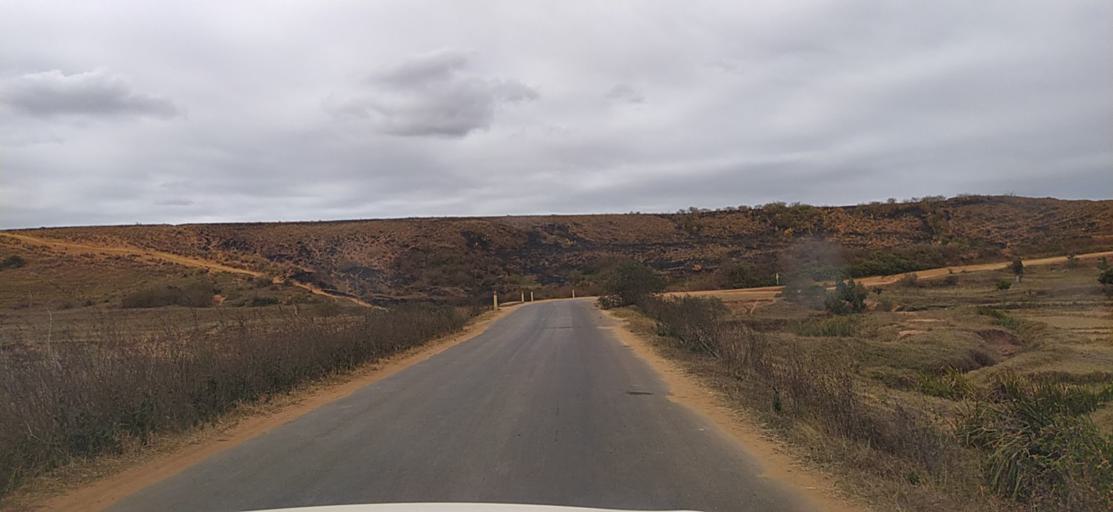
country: MG
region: Alaotra Mangoro
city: Ambatondrazaka
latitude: -17.9127
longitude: 48.2610
